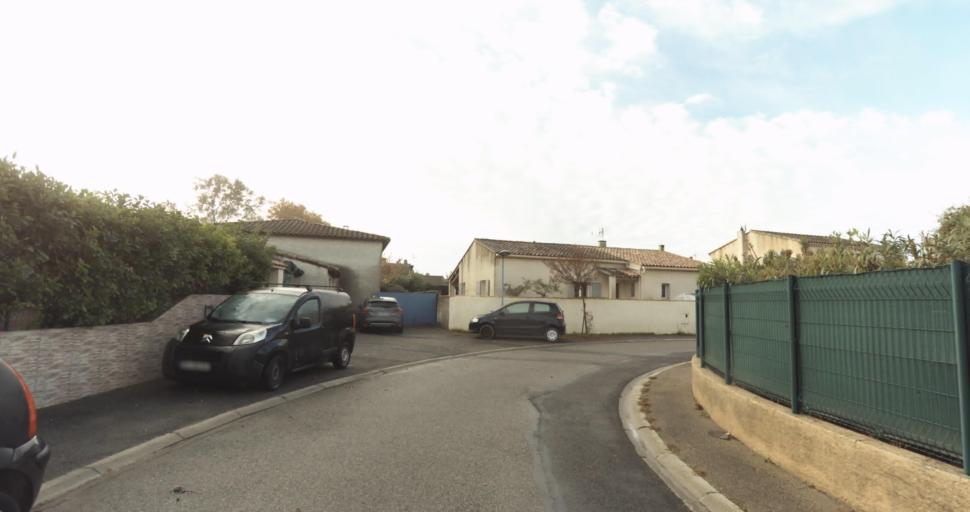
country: FR
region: Provence-Alpes-Cote d'Azur
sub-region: Departement des Bouches-du-Rhone
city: Rognonas
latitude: 43.9080
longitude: 4.8044
